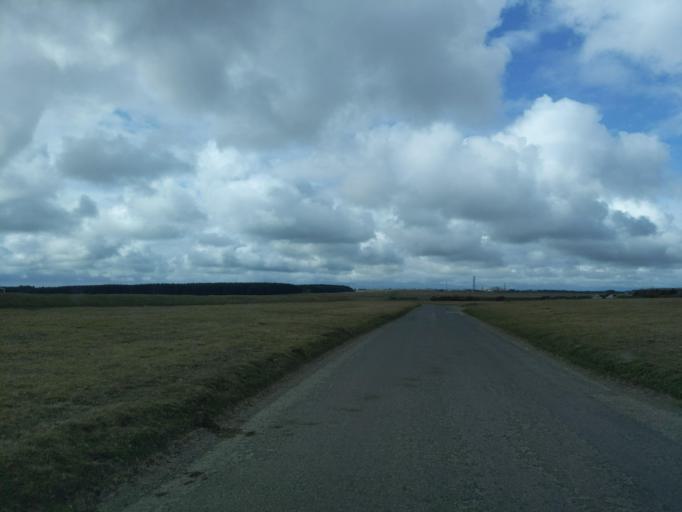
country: GB
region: England
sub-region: Cornwall
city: Camelford
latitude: 50.6295
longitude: -4.6023
